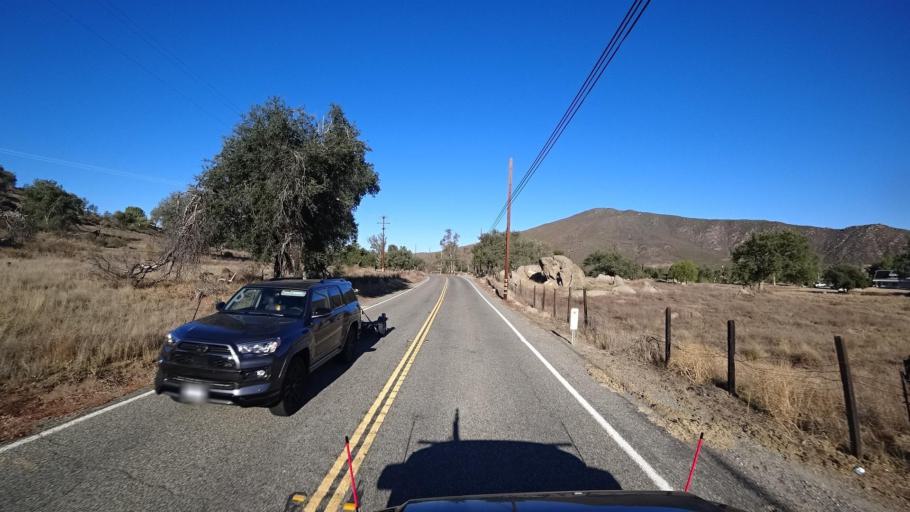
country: MX
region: Baja California
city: Tecate
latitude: 32.6070
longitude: -116.6210
